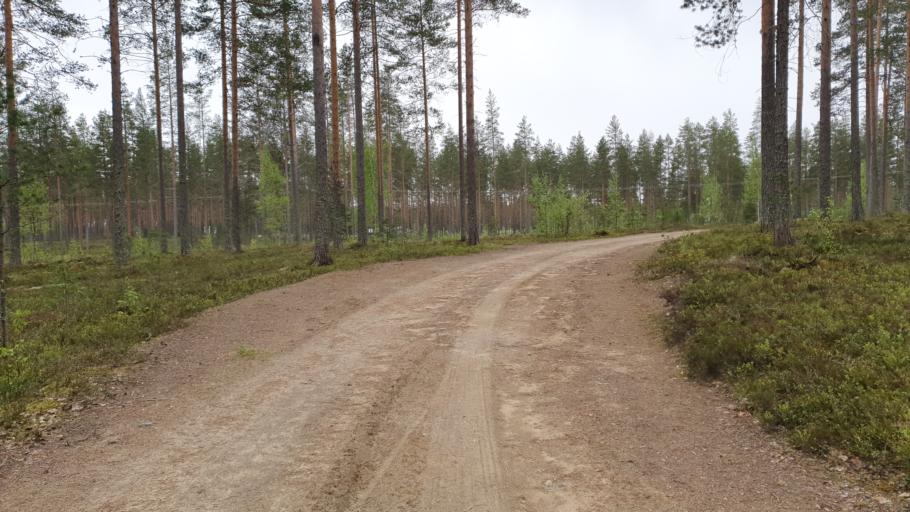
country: FI
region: Kainuu
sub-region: Kehys-Kainuu
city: Kuhmo
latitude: 64.0978
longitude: 29.4659
